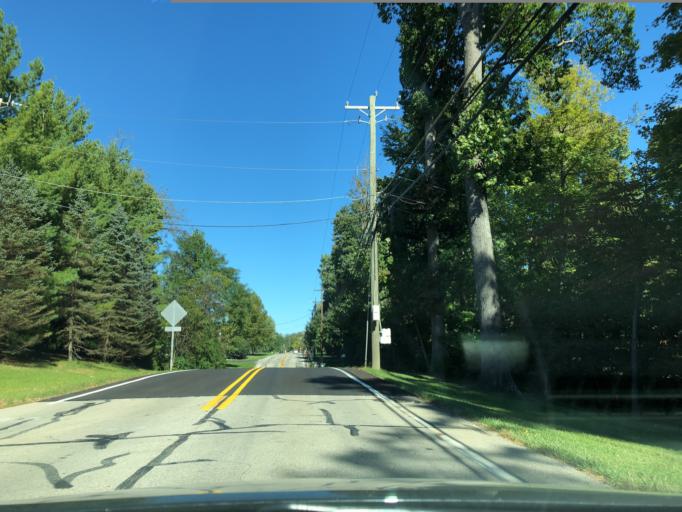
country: US
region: Ohio
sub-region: Hamilton County
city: Sixteen Mile Stand
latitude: 39.2691
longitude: -84.3067
